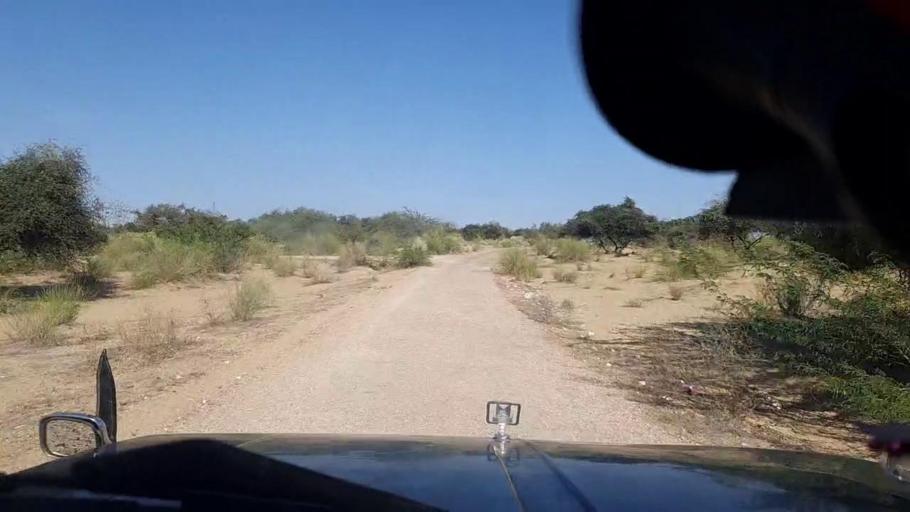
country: PK
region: Sindh
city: Diplo
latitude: 24.4703
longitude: 69.8018
